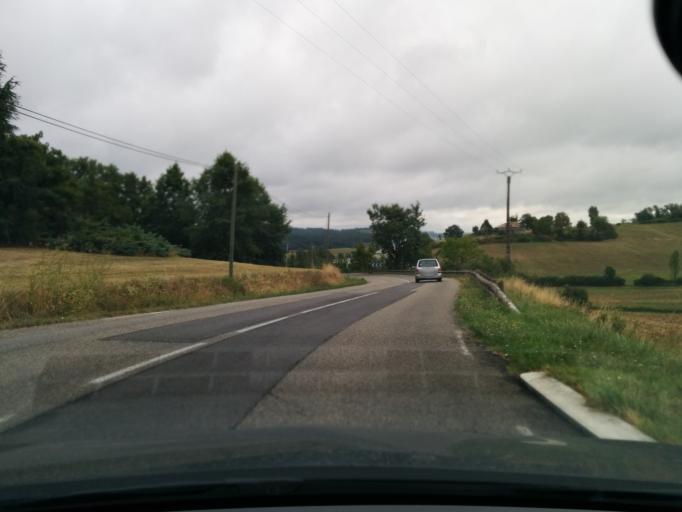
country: FR
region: Midi-Pyrenees
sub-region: Departement du Tarn-et-Garonne
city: Lauzerte
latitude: 44.1955
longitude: 1.0717
